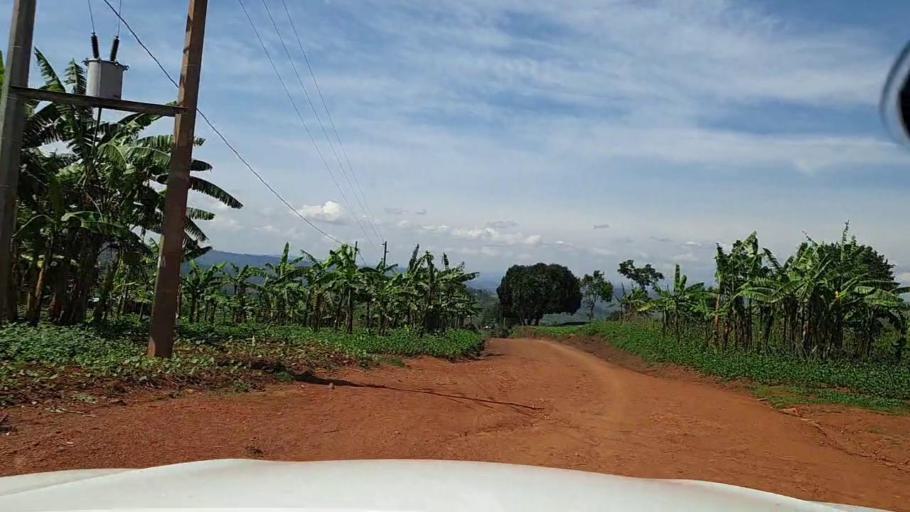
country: RW
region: Southern Province
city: Butare
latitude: -2.7213
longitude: 29.8365
